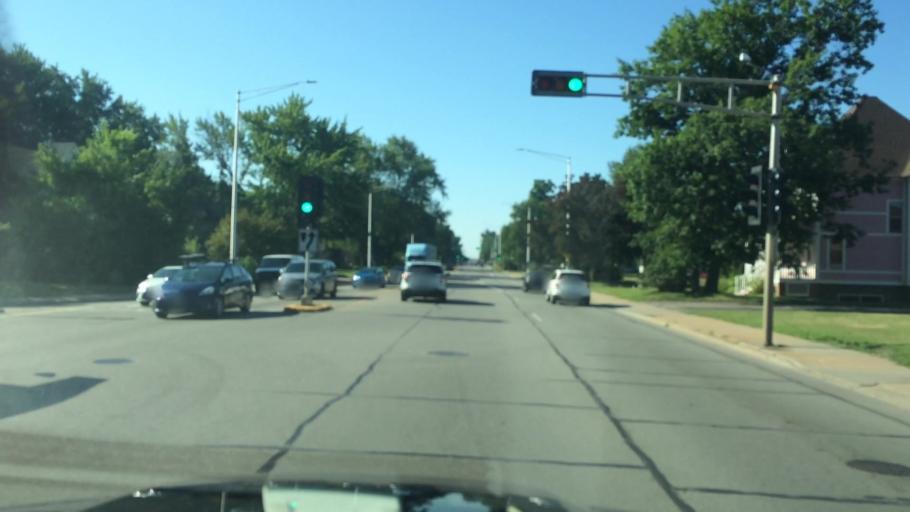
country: US
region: Wisconsin
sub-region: Marathon County
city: Wausau
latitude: 44.9450
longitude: -89.6205
